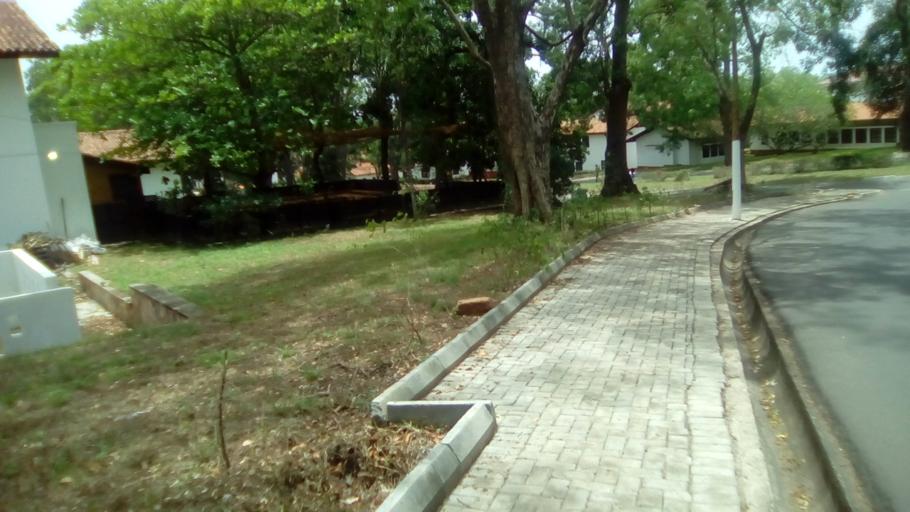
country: GH
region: Greater Accra
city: Medina Estates
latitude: 5.6511
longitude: -0.1904
